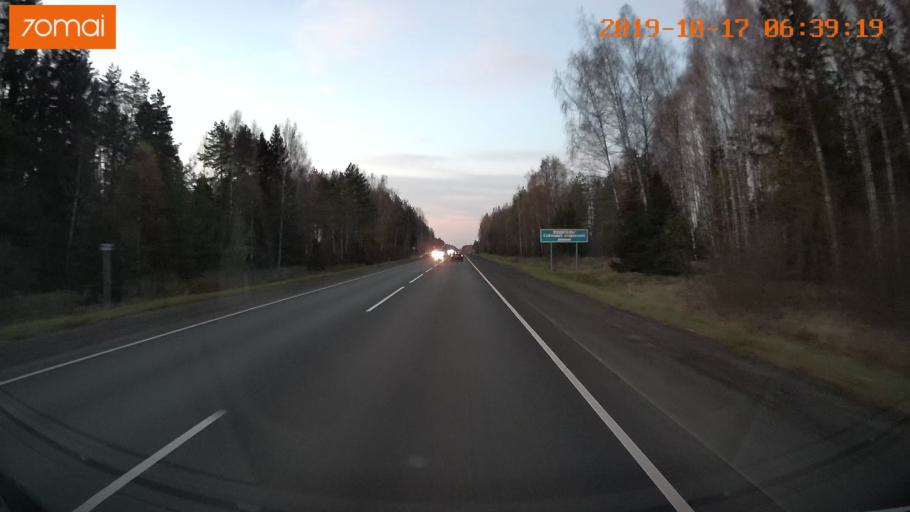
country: RU
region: Ivanovo
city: Novoye Leushino
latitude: 56.6446
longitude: 40.5798
